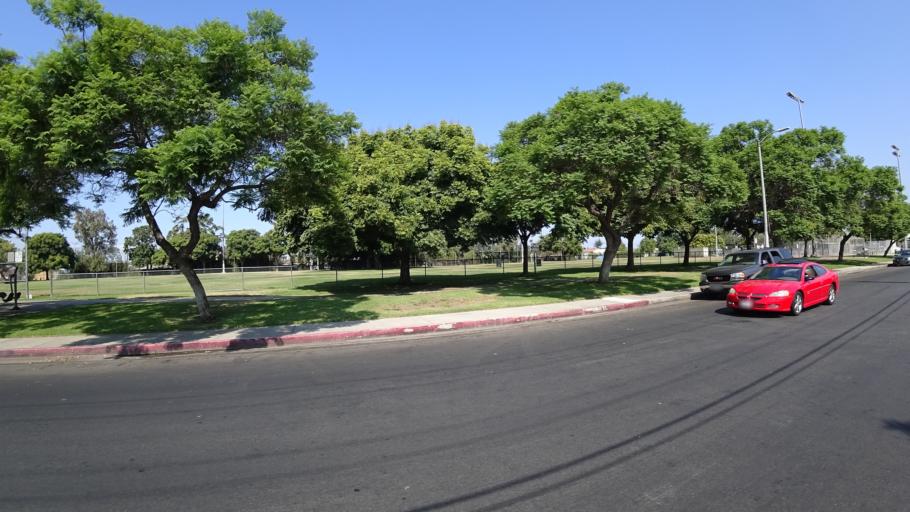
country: US
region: California
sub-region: Los Angeles County
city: Westmont
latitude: 33.9572
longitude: -118.3112
